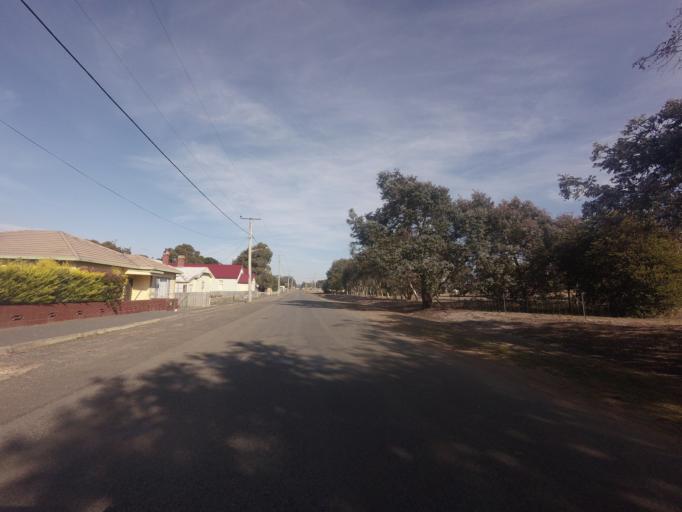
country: AU
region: Tasmania
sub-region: Sorell
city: Sorell
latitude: -42.4554
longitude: 147.4615
